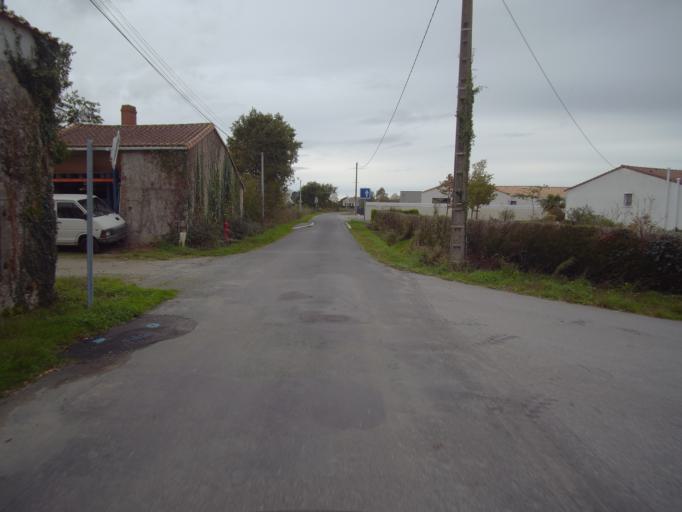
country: FR
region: Pays de la Loire
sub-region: Departement de la Loire-Atlantique
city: Remouille
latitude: 47.0311
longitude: -1.3900
